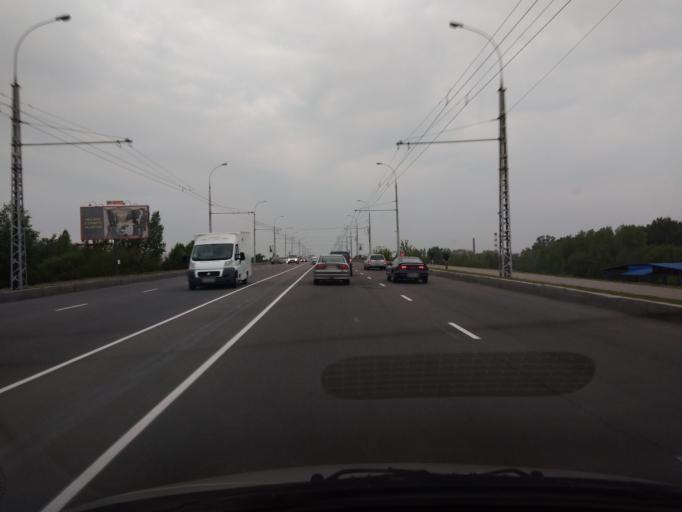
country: BY
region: Brest
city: Brest
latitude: 52.0843
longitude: 23.7361
